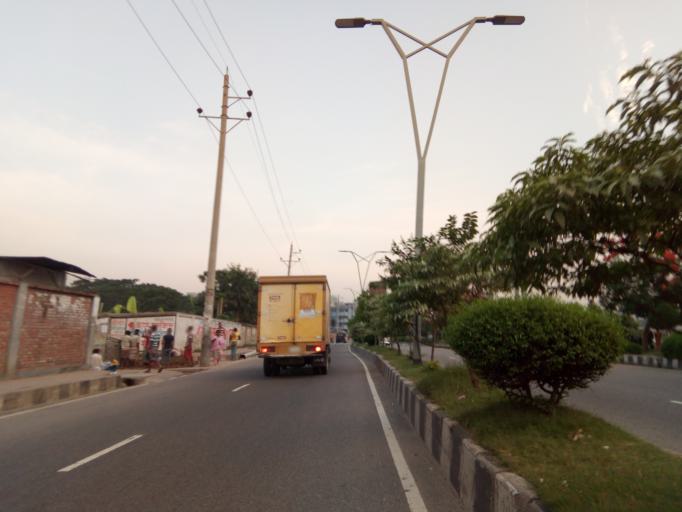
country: BD
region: Dhaka
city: Paltan
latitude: 23.7552
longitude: 90.4043
